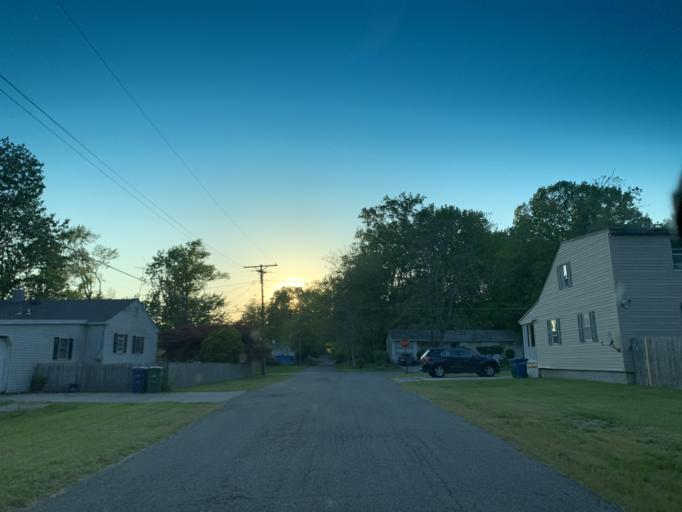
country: US
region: Maryland
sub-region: Harford County
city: Aberdeen
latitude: 39.5043
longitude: -76.1717
